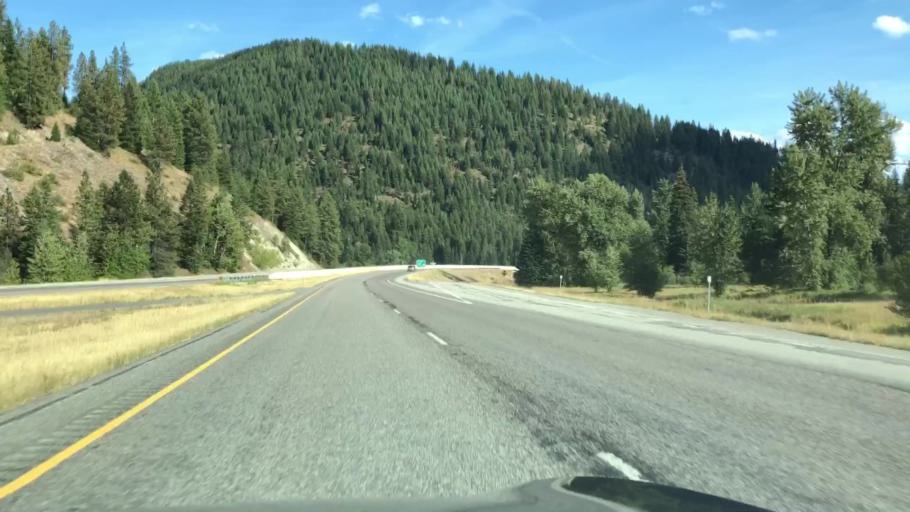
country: US
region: Montana
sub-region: Sanders County
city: Thompson Falls
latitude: 47.3561
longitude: -115.2981
